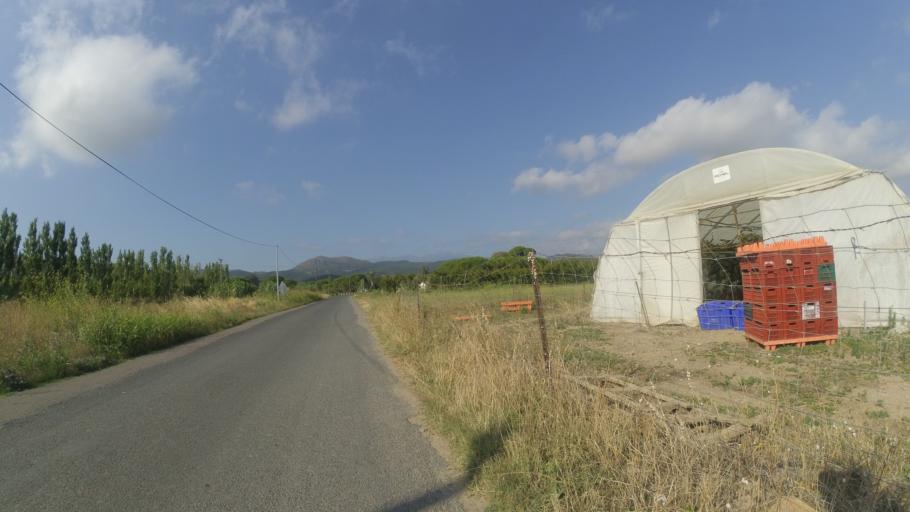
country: FR
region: Languedoc-Roussillon
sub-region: Departement des Pyrenees-Orientales
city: Millas
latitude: 42.6515
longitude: 2.7077
